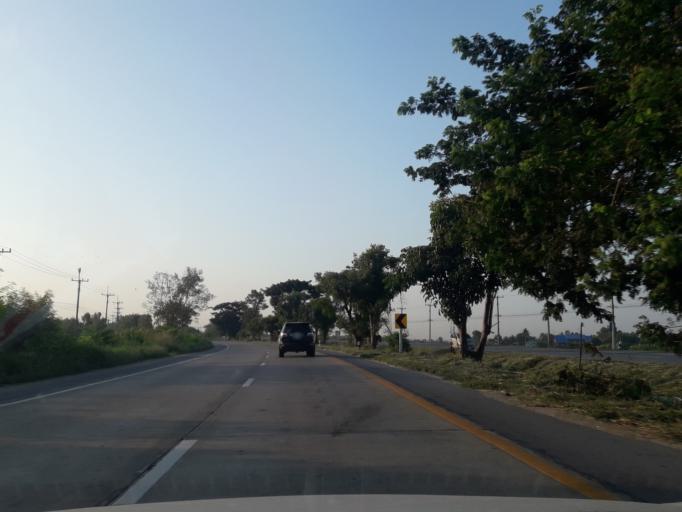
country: TH
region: Phra Nakhon Si Ayutthaya
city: Phra Nakhon Si Ayutthaya
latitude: 14.2928
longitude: 100.5243
